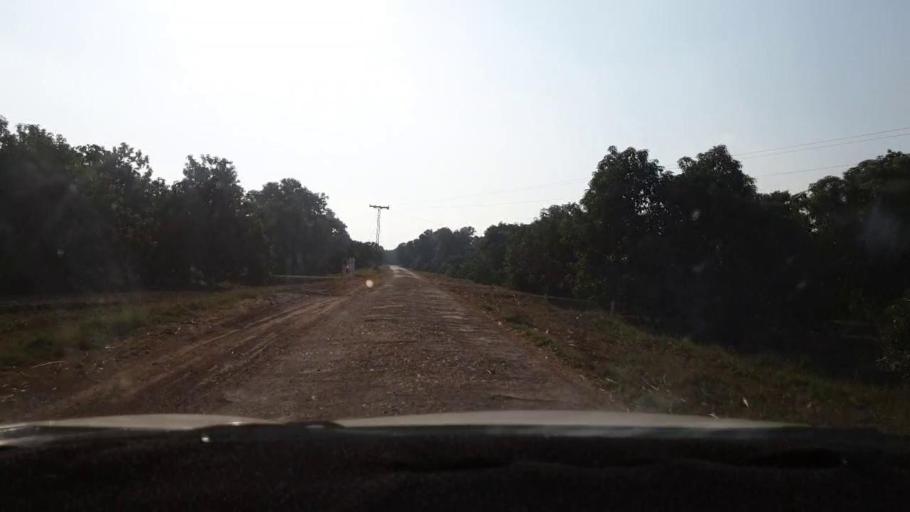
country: PK
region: Sindh
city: Berani
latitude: 25.7622
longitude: 68.7610
